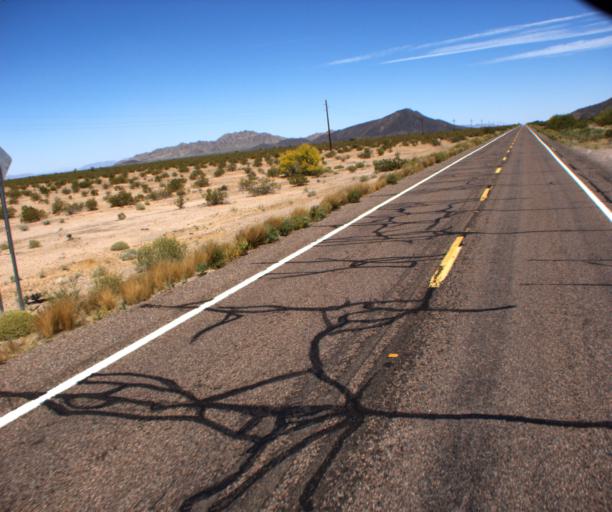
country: US
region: Arizona
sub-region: Maricopa County
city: Gila Bend
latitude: 32.7222
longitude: -112.8390
